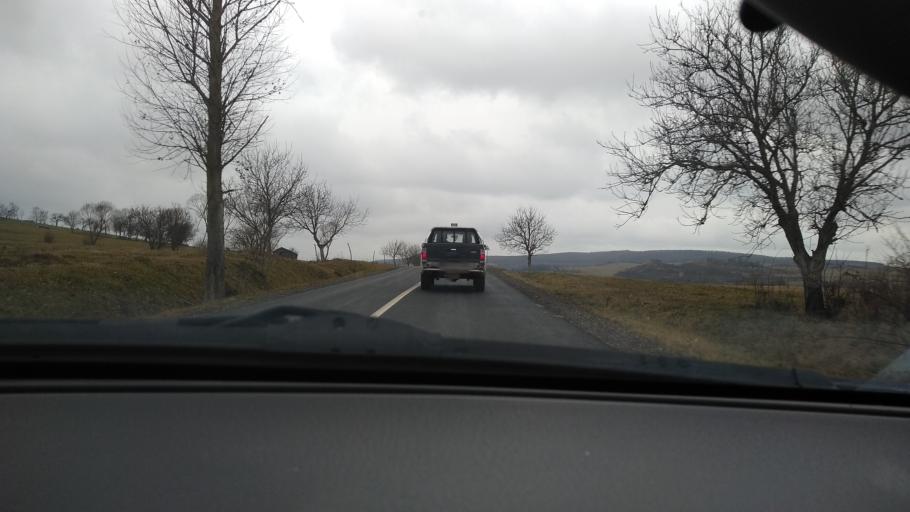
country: RO
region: Mures
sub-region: Comuna Bereni
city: Bereni
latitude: 46.5586
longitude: 24.8844
